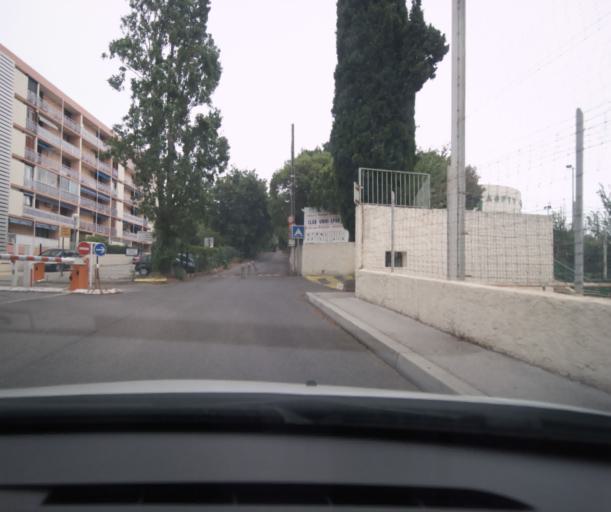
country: FR
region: Provence-Alpes-Cote d'Azur
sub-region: Departement du Var
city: La Valette-du-Var
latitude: 43.1265
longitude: 5.9866
